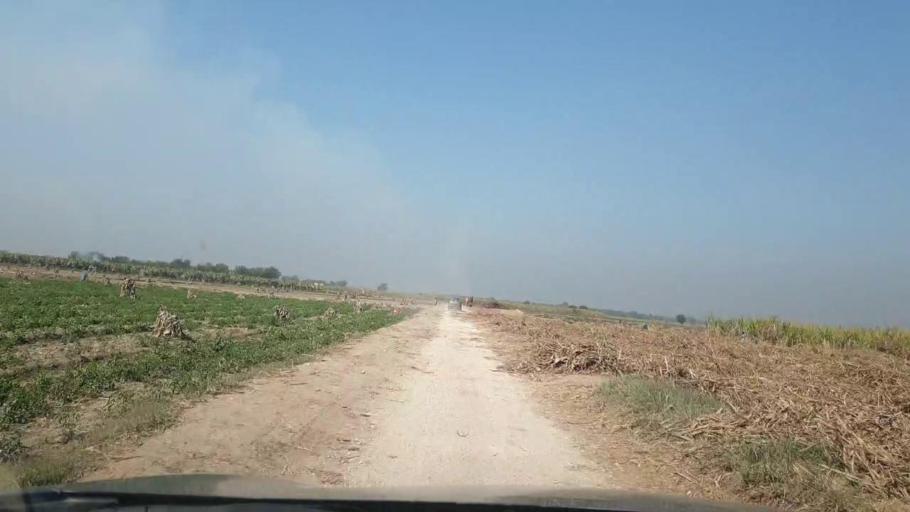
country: PK
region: Sindh
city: Tando Allahyar
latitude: 25.4746
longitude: 68.6415
